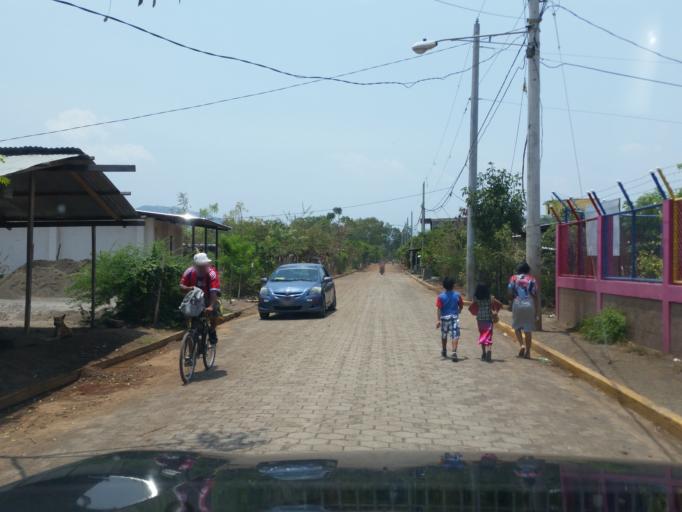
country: NI
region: Granada
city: Granada
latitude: 11.9099
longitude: -85.9615
